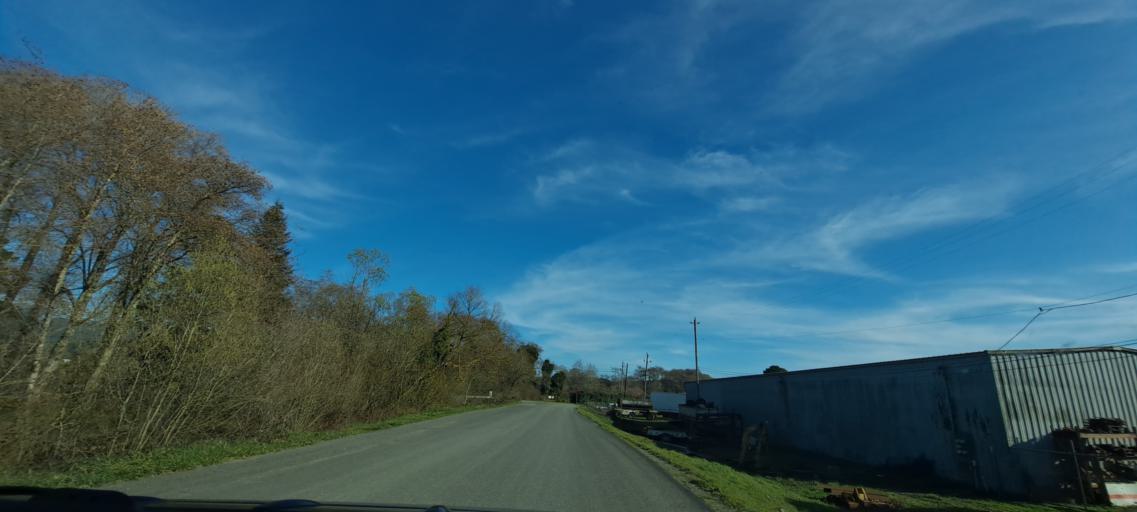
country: US
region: California
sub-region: Humboldt County
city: Fortuna
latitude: 40.5856
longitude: -124.1555
